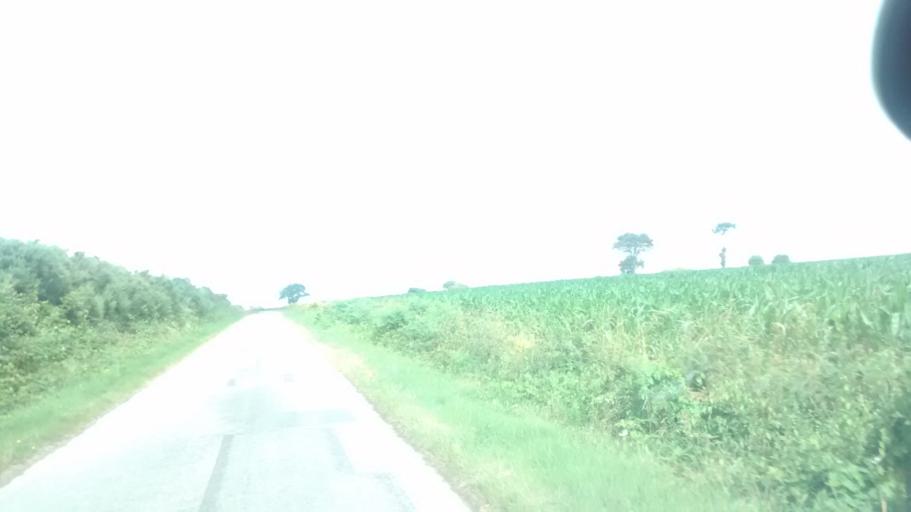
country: FR
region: Brittany
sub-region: Departement d'Ille-et-Vilaine
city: Grand-Fougeray
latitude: 47.7782
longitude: -1.7458
